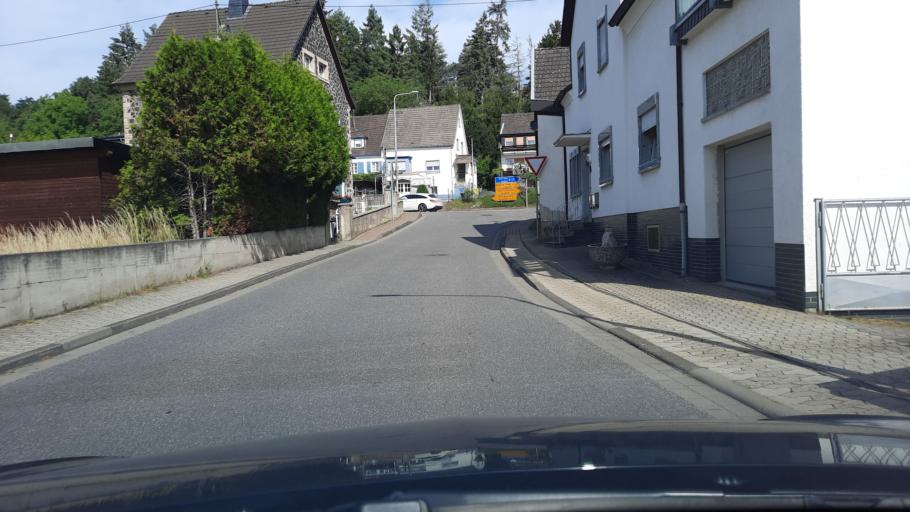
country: DE
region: Rheinland-Pfalz
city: Oberzissen
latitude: 50.4583
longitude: 7.2151
